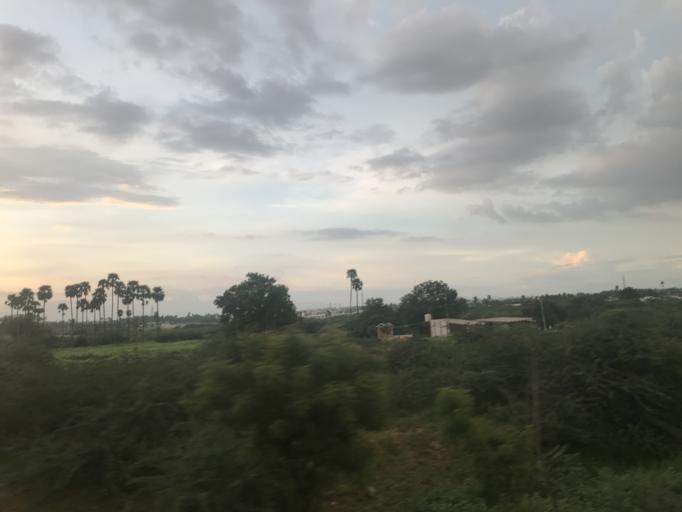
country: IN
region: Tamil Nadu
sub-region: Tiruppur
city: Tiruppur
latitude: 11.1308
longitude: 77.3709
